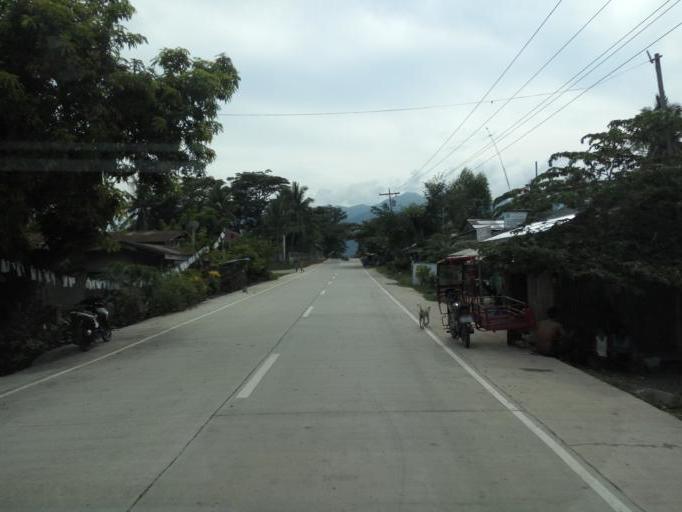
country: PH
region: Central Luzon
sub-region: Province of Aurora
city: Dinalongan
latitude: 16.0774
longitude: 121.7718
